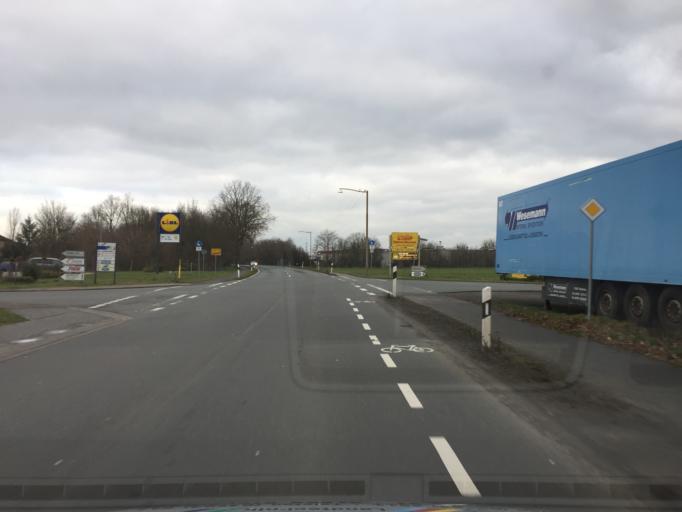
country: DE
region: Lower Saxony
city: Stolzenau
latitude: 52.5225
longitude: 9.0759
